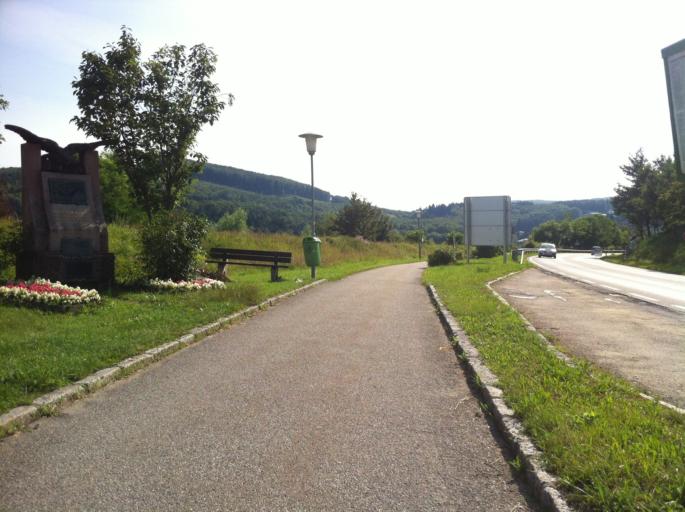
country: AT
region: Lower Austria
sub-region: Politischer Bezirk Wien-Umgebung
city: Wolfsgraben
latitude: 48.1835
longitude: 16.1211
